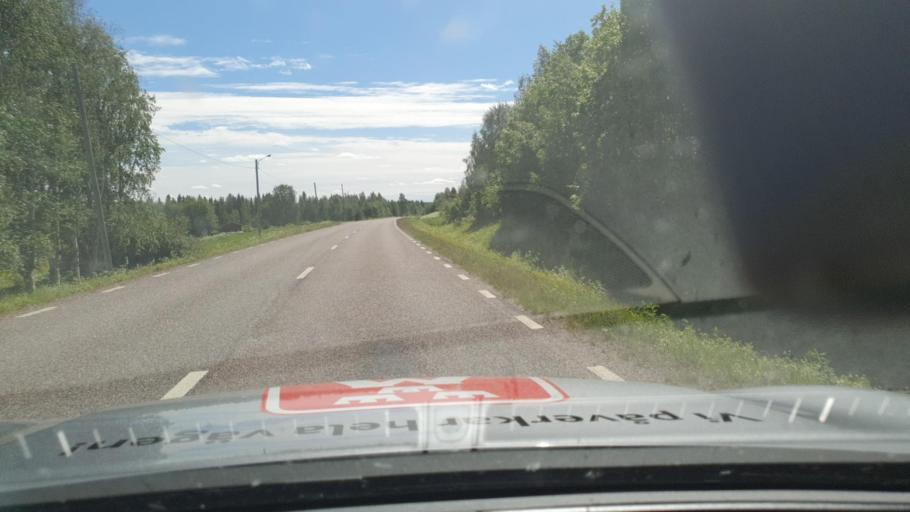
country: FI
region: Lapland
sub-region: Torniolaakso
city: Pello
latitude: 66.9432
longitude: 23.8511
